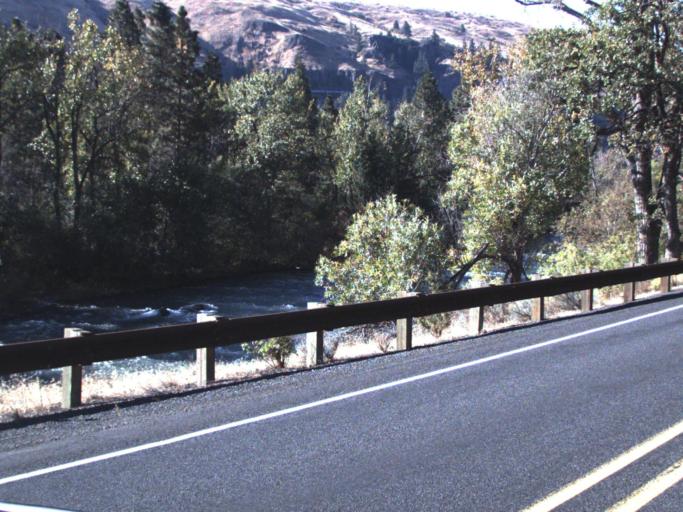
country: US
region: Washington
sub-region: Yakima County
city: Tieton
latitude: 46.7212
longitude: -120.8469
